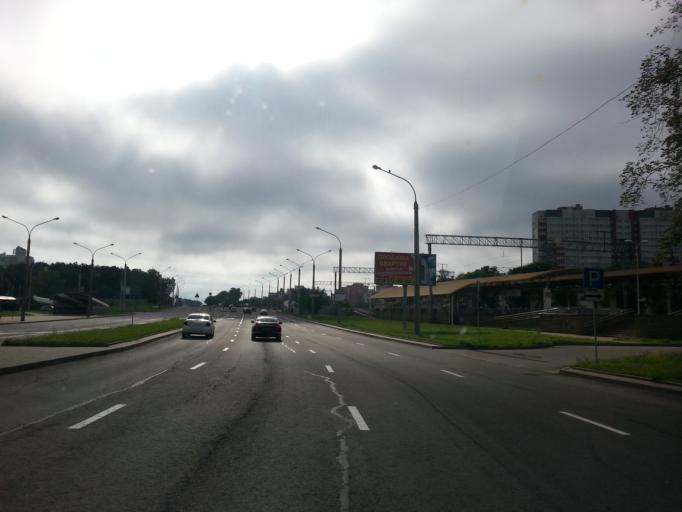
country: BY
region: Minsk
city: Zhdanovichy
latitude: 53.9307
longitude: 27.4750
